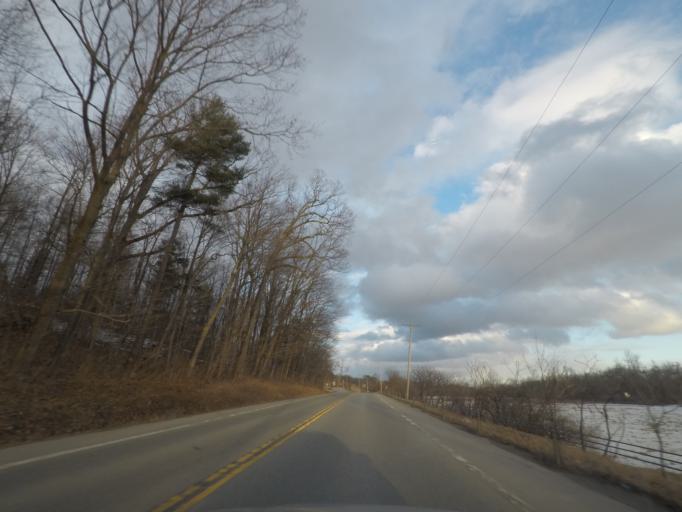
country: US
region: New York
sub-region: Montgomery County
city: Saint Johnsville
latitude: 43.0065
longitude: -74.7484
